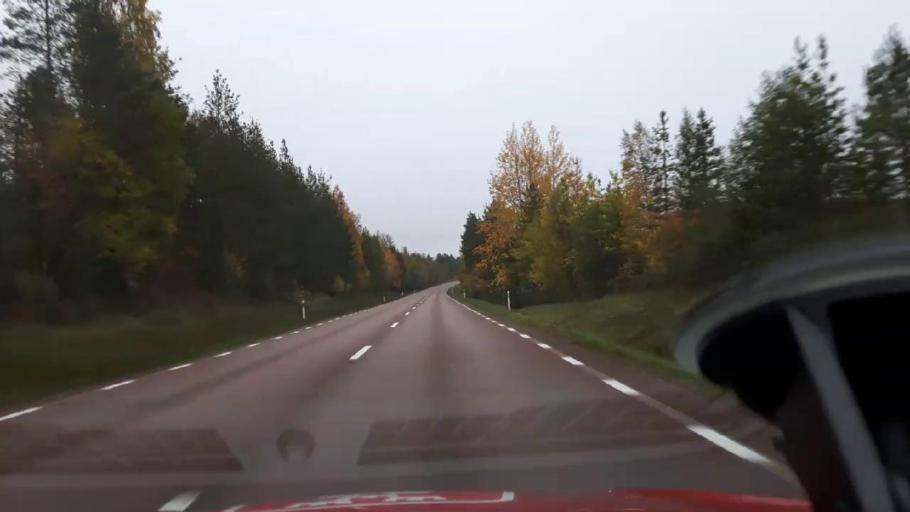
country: SE
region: Jaemtland
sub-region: Bergs Kommun
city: Hoverberg
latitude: 62.5185
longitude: 14.4487
